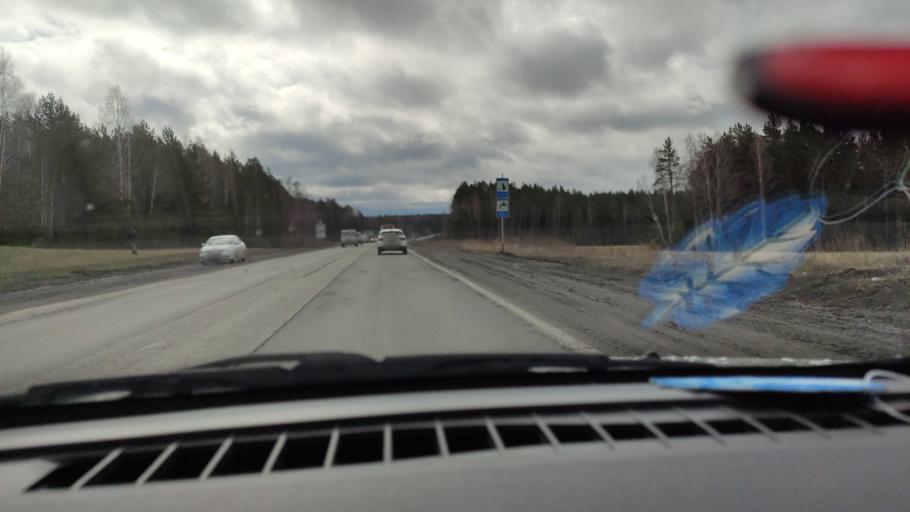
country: RU
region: Sverdlovsk
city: Talitsa
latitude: 56.8670
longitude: 60.0455
